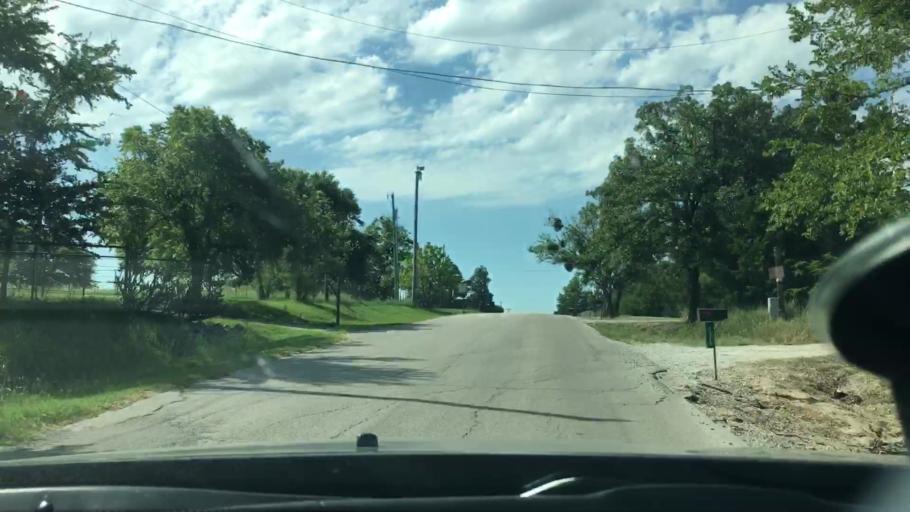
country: US
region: Oklahoma
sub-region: Carter County
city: Ardmore
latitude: 34.1448
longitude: -97.0905
